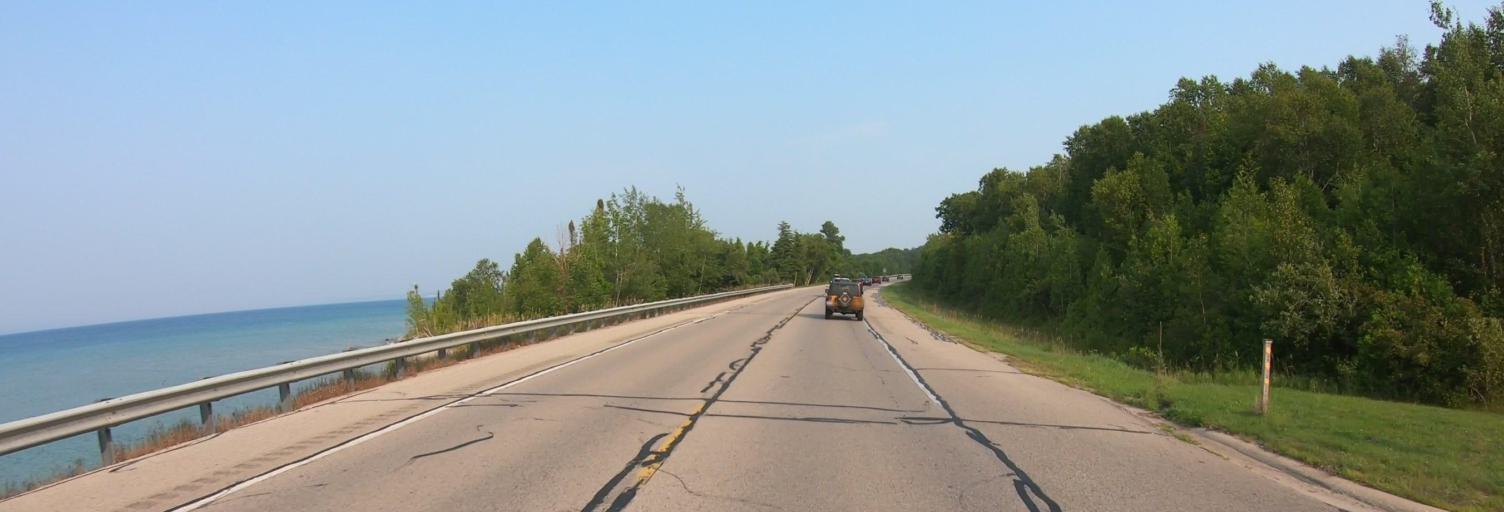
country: US
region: Michigan
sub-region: Charlevoix County
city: Charlevoix
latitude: 45.3672
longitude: -85.1278
